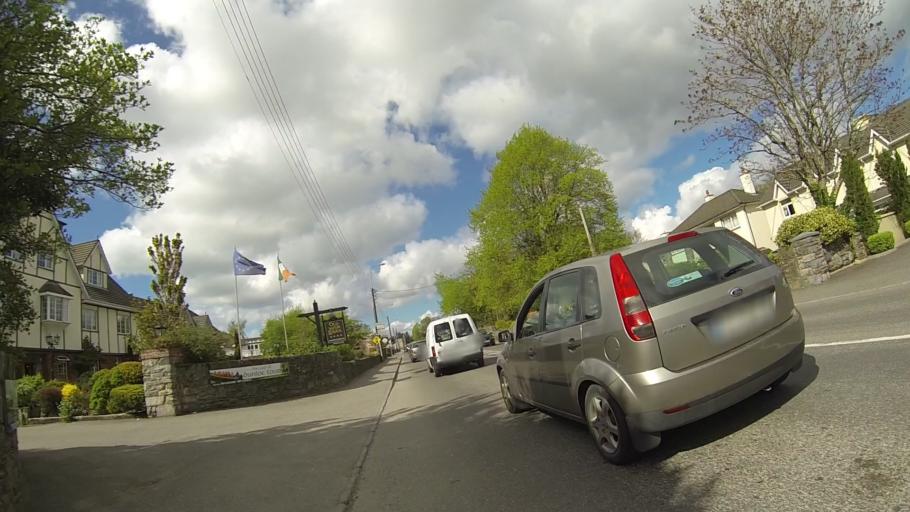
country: IE
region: Munster
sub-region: Ciarrai
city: Cill Airne
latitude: 52.0514
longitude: -9.5068
